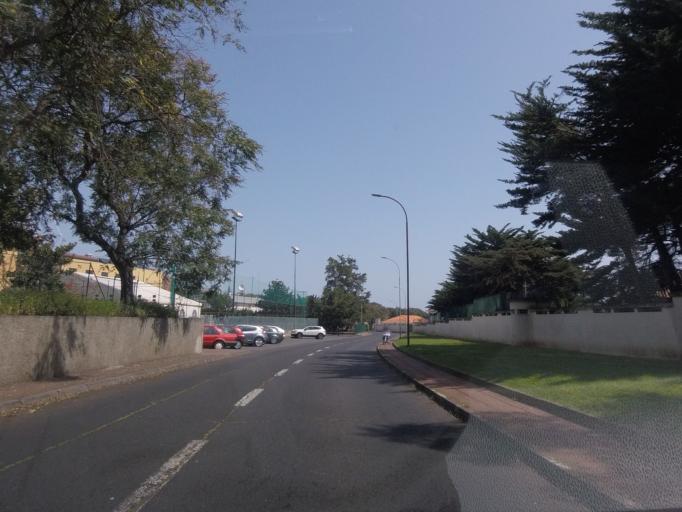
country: PT
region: Madeira
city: Camara de Lobos
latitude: 32.6446
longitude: -16.9366
